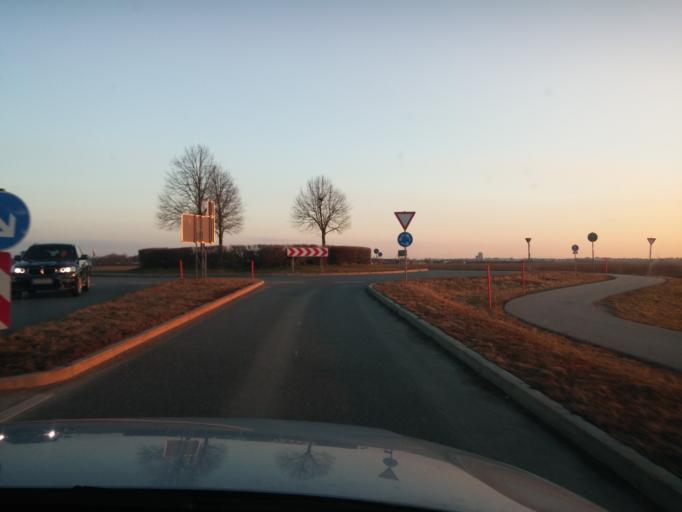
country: DE
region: Bavaria
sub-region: Upper Bavaria
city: Feldkirchen
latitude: 48.1392
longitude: 11.7361
